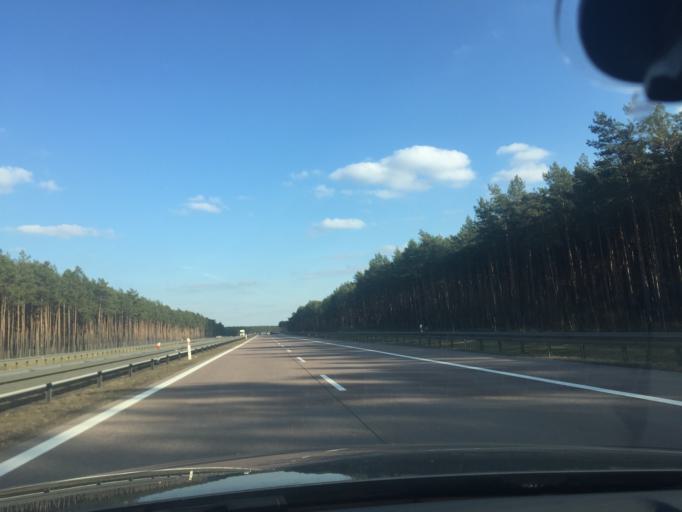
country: PL
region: Lubusz
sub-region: Powiat slubicki
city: Rzepin
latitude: 52.3353
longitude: 14.7836
